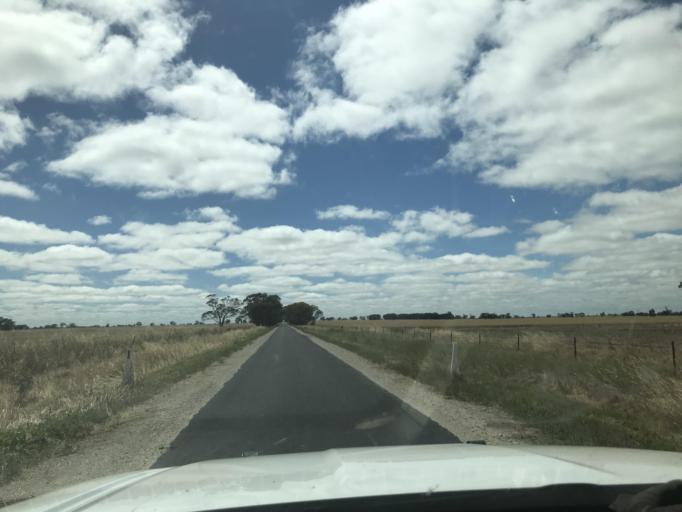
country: AU
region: South Australia
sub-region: Tatiara
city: Bordertown
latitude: -36.2778
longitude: 141.1088
